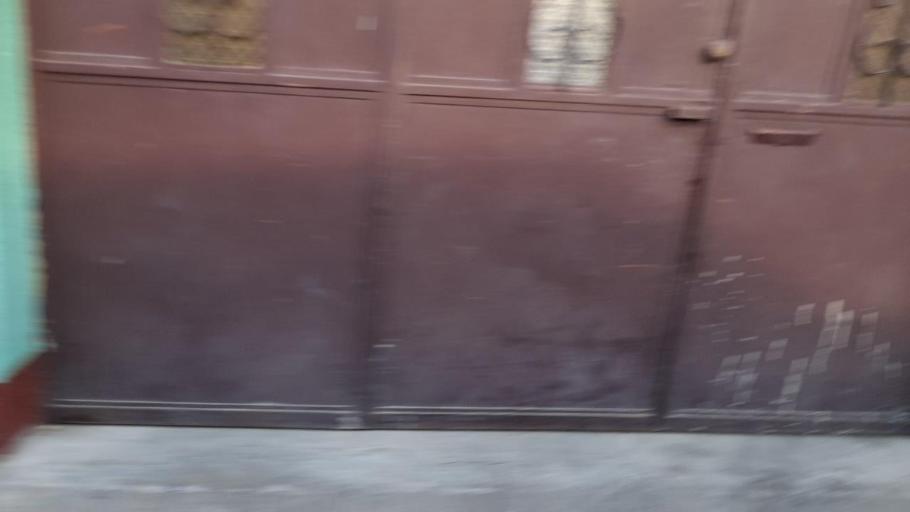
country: GT
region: Quetzaltenango
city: Quetzaltenango
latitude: 14.8281
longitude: -91.5170
